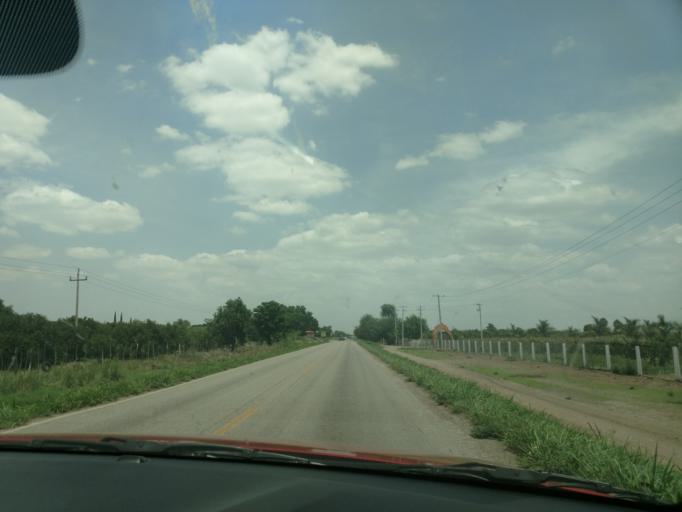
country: MX
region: San Luis Potosi
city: Ciudad Fernandez
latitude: 21.9537
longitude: -100.0683
